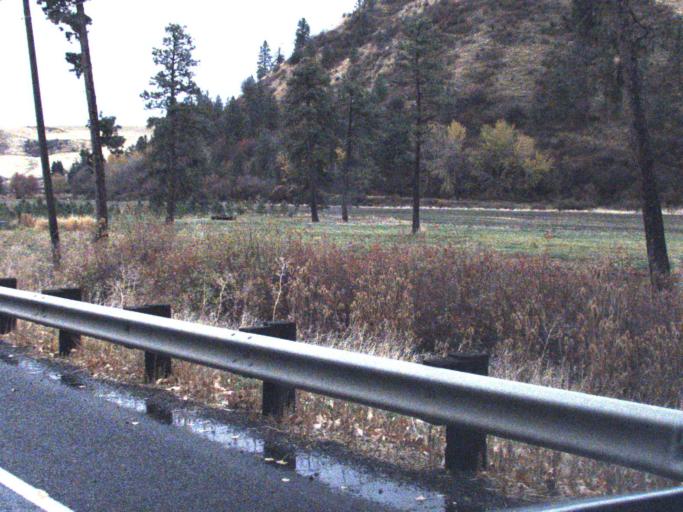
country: US
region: Washington
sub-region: Walla Walla County
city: Waitsburg
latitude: 46.2889
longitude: -118.0802
